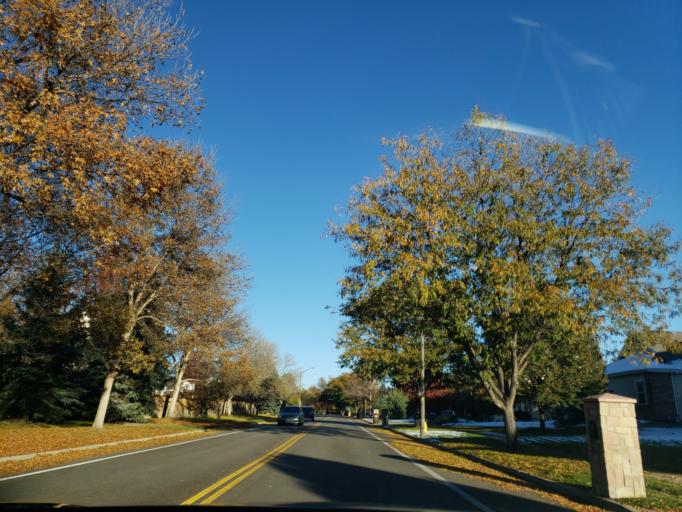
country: US
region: Colorado
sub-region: Larimer County
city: Fort Collins
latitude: 40.5010
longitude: -105.0622
